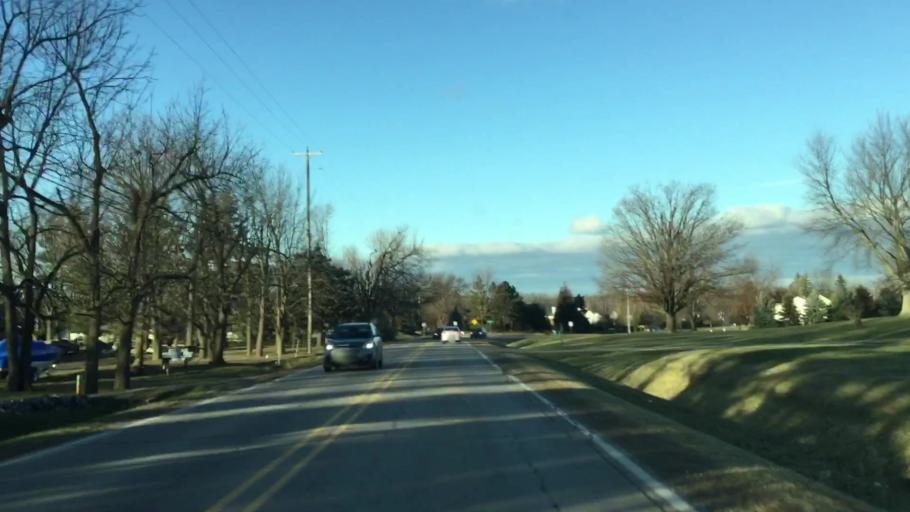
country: US
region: Michigan
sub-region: Genesee County
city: Linden
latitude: 42.7967
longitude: -83.7866
